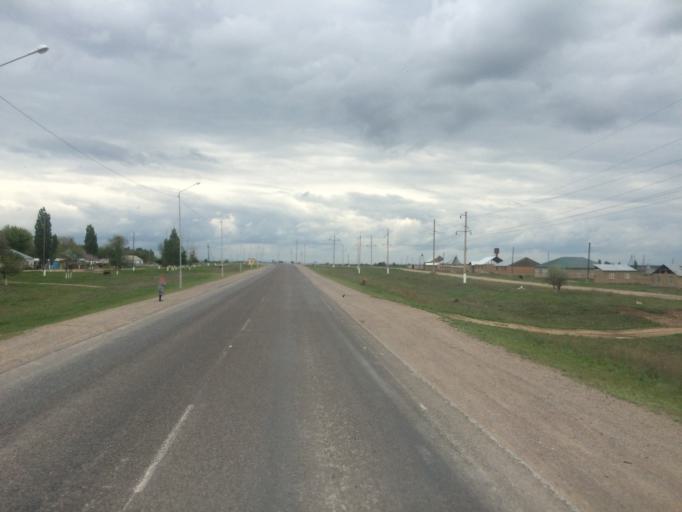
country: KG
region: Chuy
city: Sokuluk
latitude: 43.2476
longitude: 74.2965
